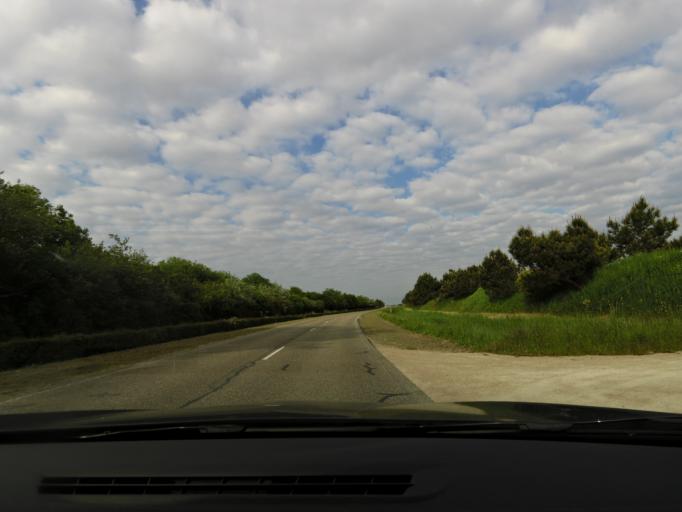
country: NL
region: South Holland
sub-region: Gemeente Goeree-Overflakkee
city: Ouddorp
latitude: 51.8185
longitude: 3.9033
